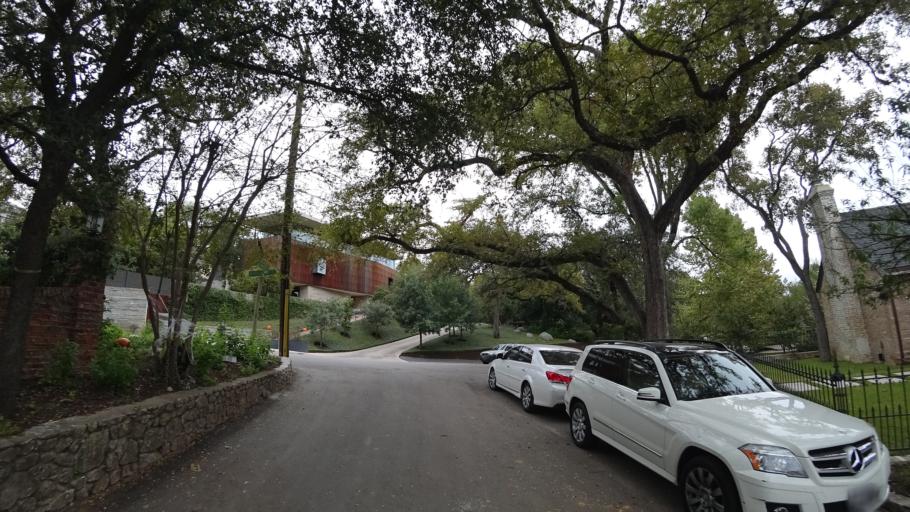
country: US
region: Texas
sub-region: Travis County
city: Austin
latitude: 30.2871
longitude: -97.7554
